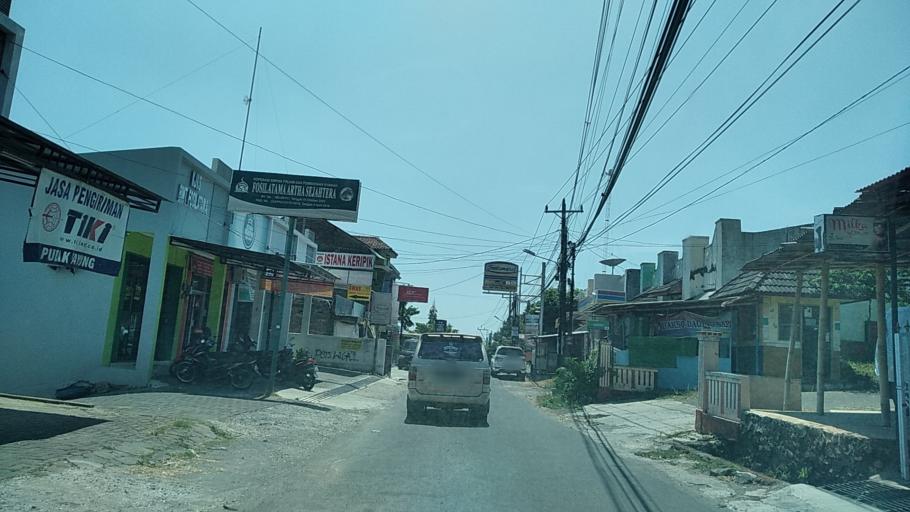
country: ID
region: Central Java
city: Ungaran
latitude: -7.0911
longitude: 110.4165
